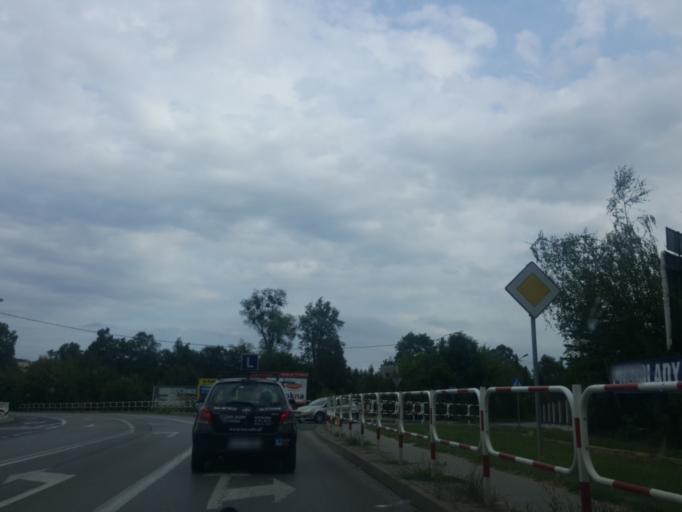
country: PL
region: Lesser Poland Voivodeship
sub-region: Powiat chrzanowski
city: Chrzanow
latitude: 50.1346
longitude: 19.4091
